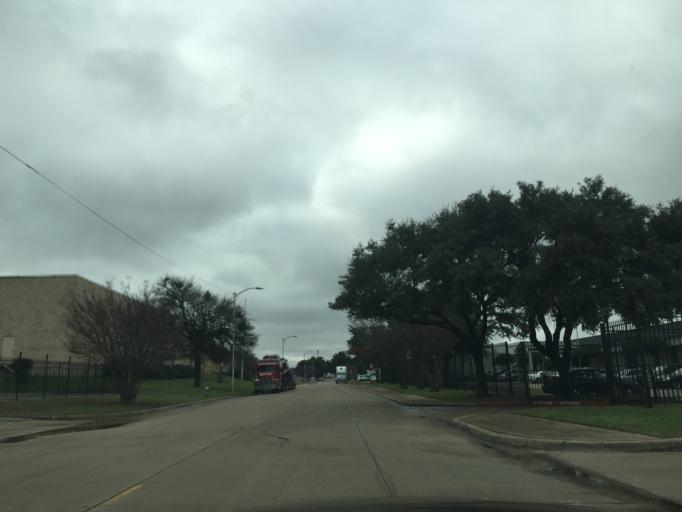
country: US
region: Texas
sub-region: Tarrant County
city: Arlington
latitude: 32.7530
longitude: -97.0600
